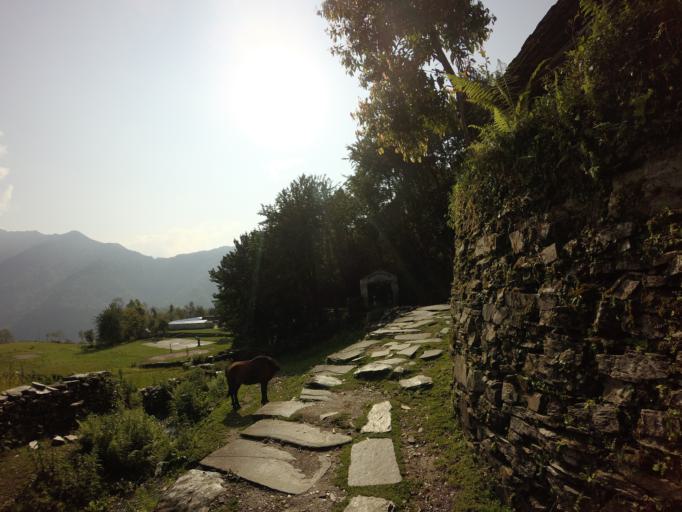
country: NP
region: Western Region
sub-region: Dhawalagiri Zone
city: Chitre
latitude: 28.3761
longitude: 83.8100
